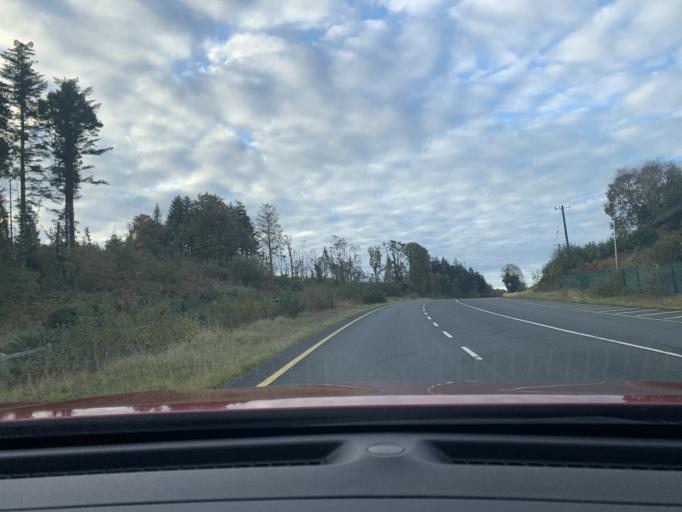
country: IE
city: Ballisodare
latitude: 54.2197
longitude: -8.4668
